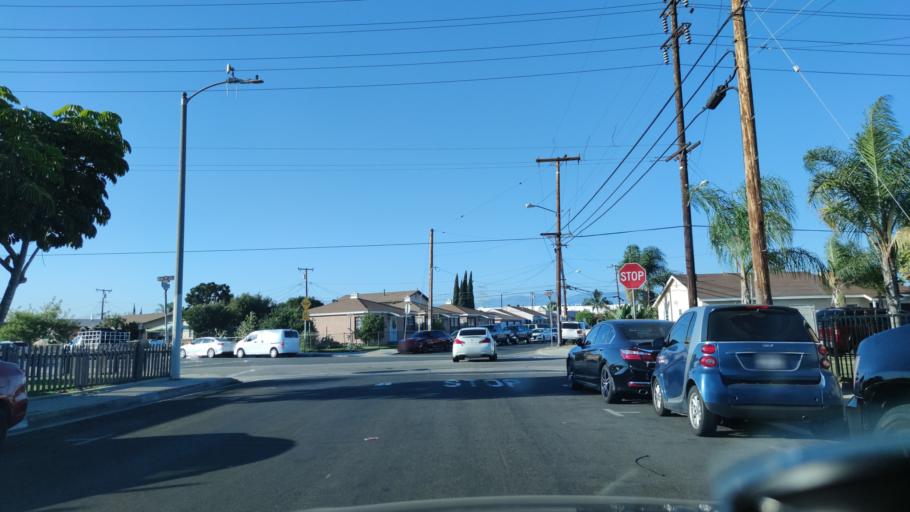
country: US
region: California
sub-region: Los Angeles County
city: Maywood
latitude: 33.9896
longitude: -118.1830
